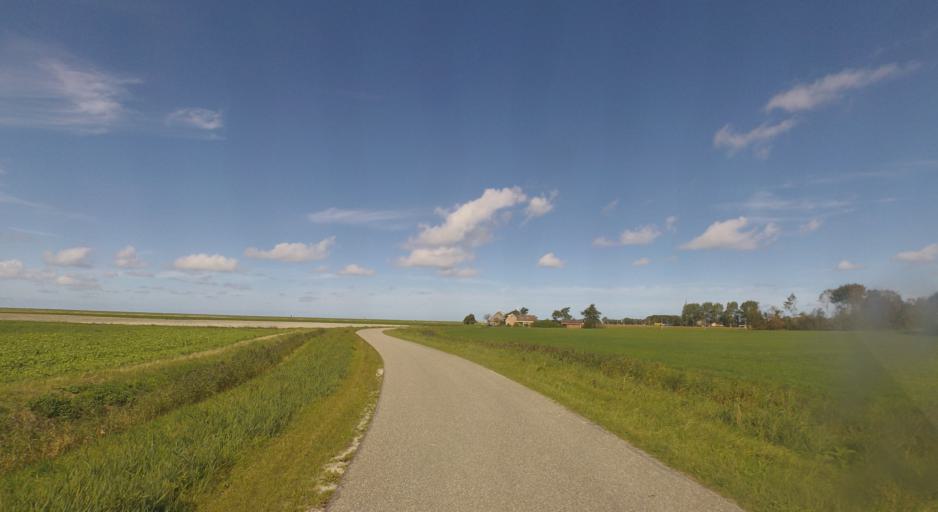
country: NL
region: Friesland
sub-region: Gemeente Dongeradeel
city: Holwerd
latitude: 53.3636
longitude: 5.8950
